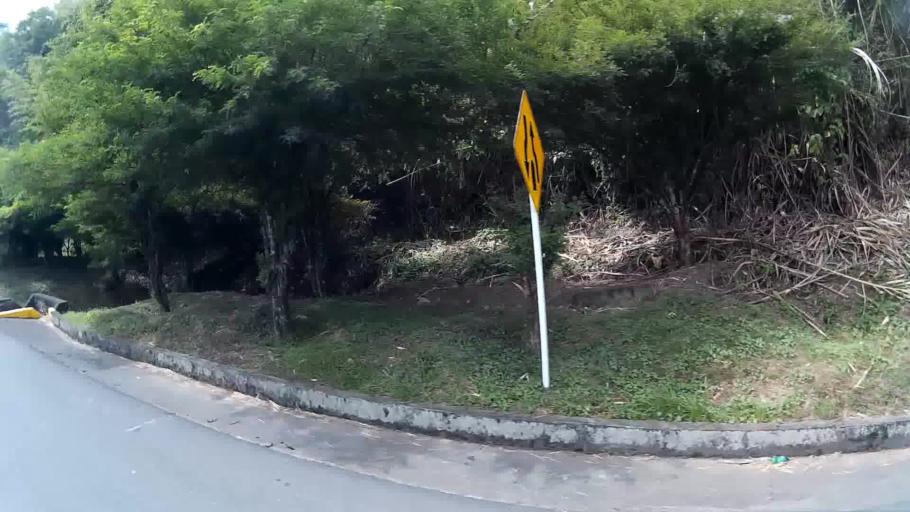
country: CO
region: Risaralda
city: Pereira
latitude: 4.8120
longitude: -75.7509
